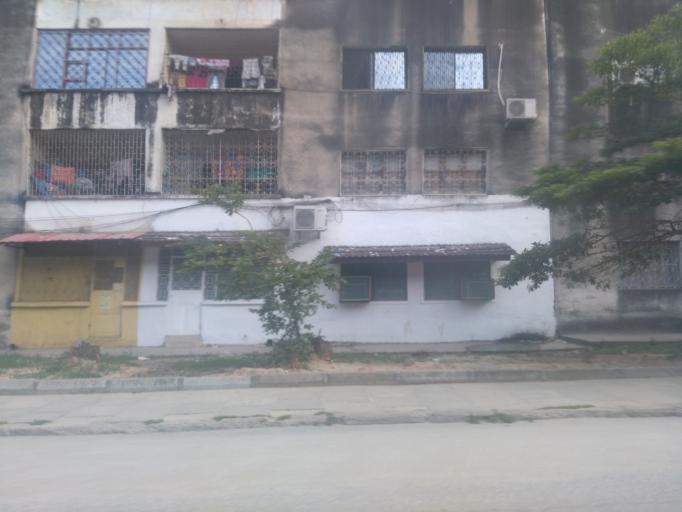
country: TZ
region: Zanzibar Urban/West
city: Zanzibar
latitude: -6.1649
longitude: 39.1980
